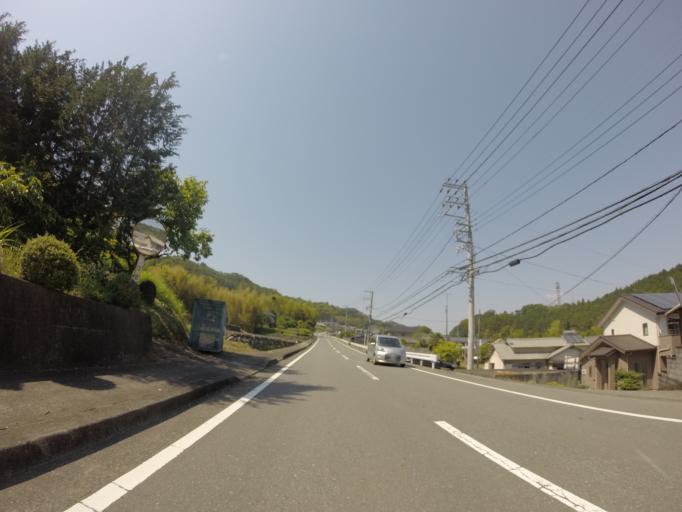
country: JP
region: Shizuoka
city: Fujinomiya
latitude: 35.2080
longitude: 138.5869
